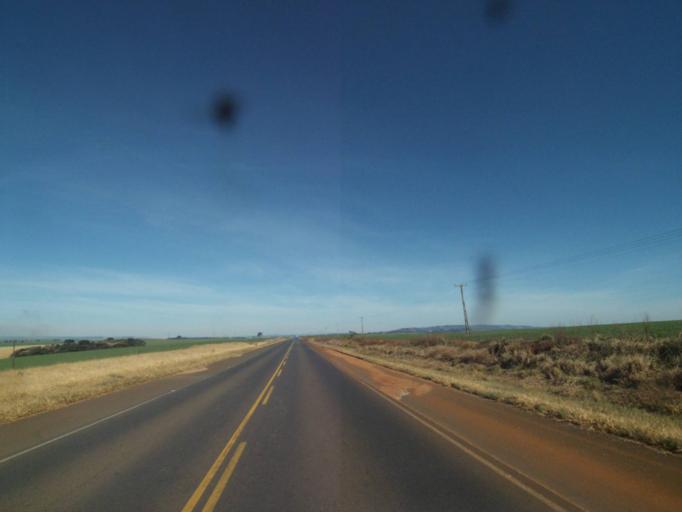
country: BR
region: Parana
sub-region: Tibagi
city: Tibagi
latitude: -24.4414
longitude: -50.4232
